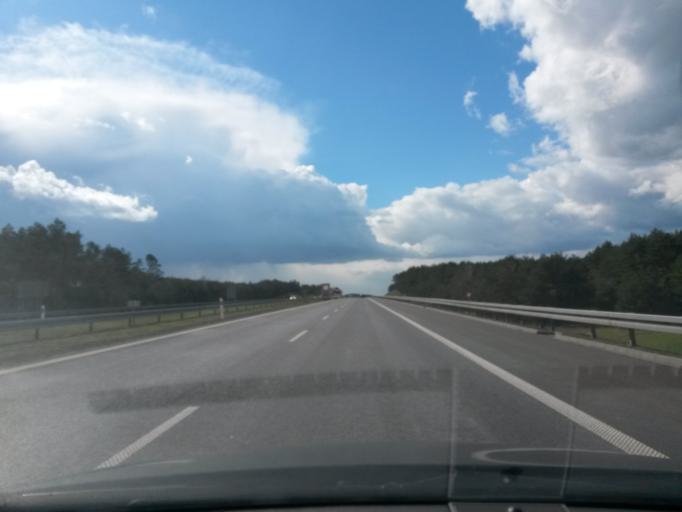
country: PL
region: Greater Poland Voivodeship
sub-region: Powiat kolski
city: Koscielec
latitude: 52.1418
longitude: 18.5584
